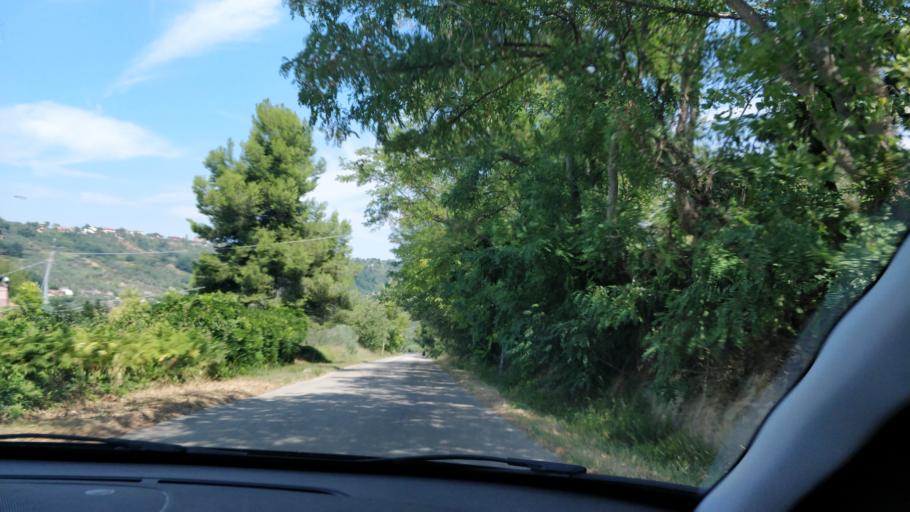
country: IT
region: Abruzzo
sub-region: Provincia di Chieti
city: Torrevecchia
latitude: 42.4047
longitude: 14.2071
